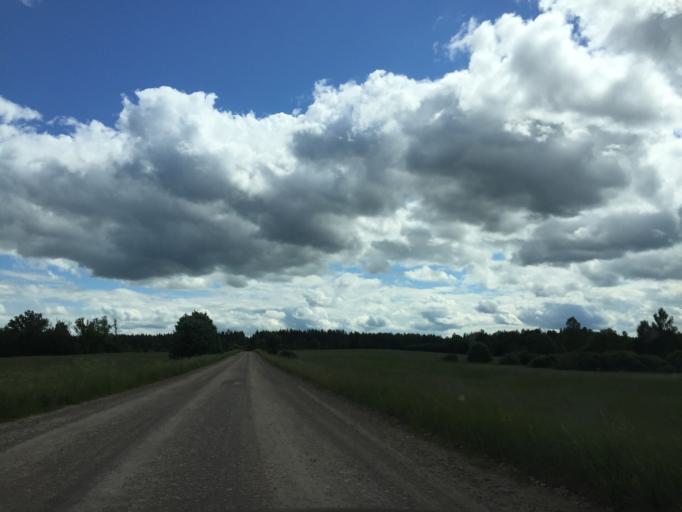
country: LV
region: Vecumnieki
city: Vecumnieki
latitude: 56.5017
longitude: 24.4064
